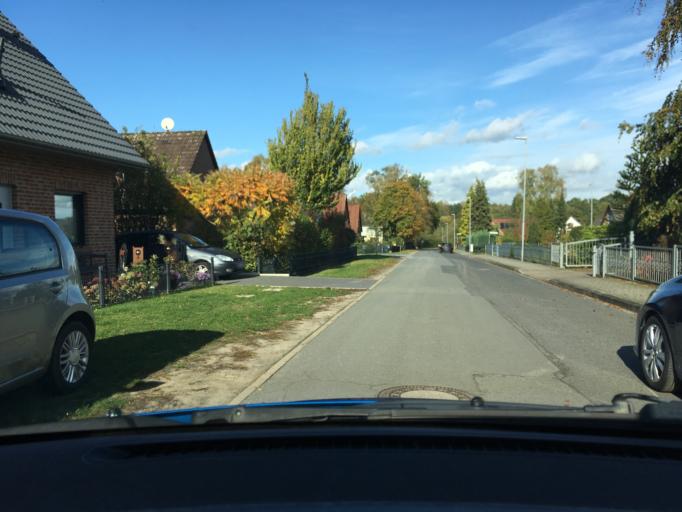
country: DE
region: Lower Saxony
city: Kakenstorf
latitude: 53.3127
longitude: 9.7878
